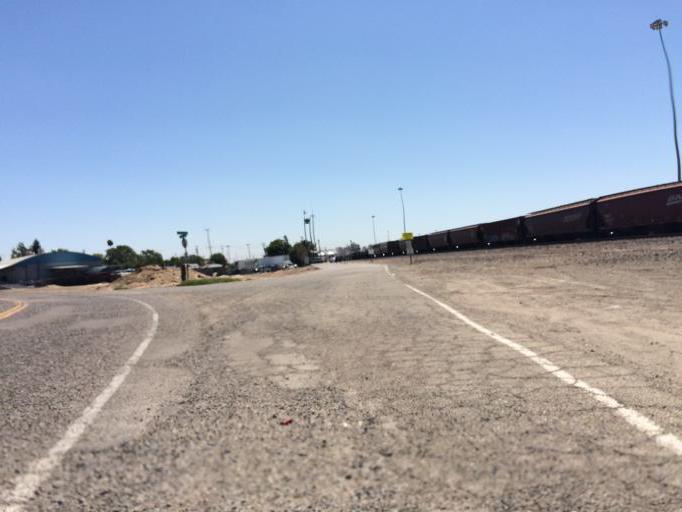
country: US
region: California
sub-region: Fresno County
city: Fresno
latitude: 36.7050
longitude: -119.7620
